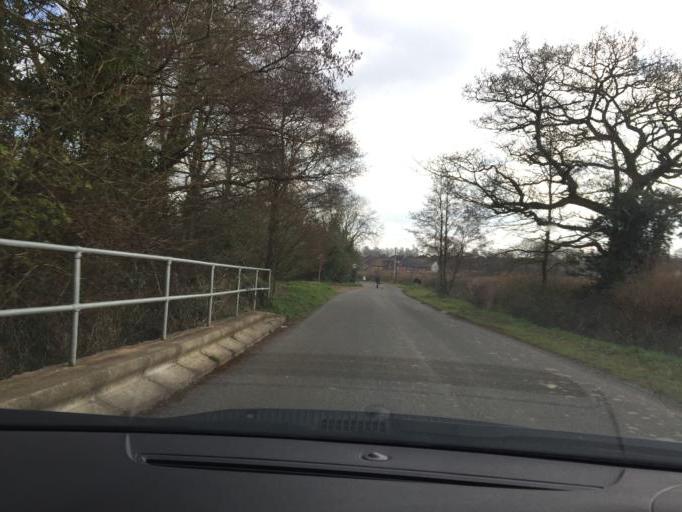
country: GB
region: England
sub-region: Coventry
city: Keresley
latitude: 52.4331
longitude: -1.5708
